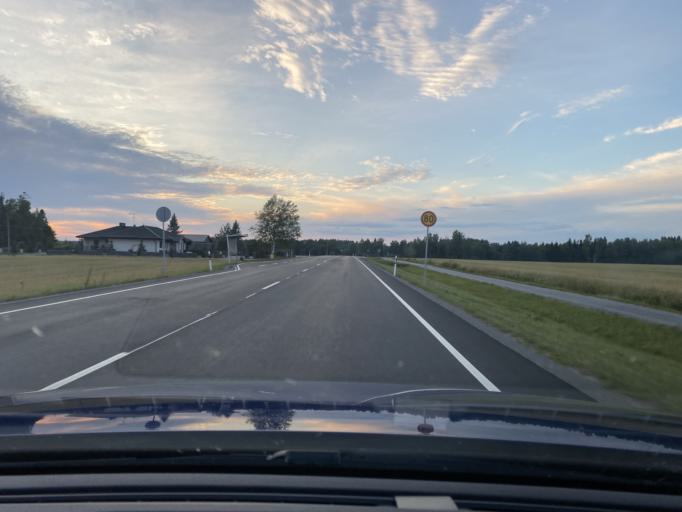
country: FI
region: Satakunta
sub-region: Pohjois-Satakunta
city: Kankaanpaeae
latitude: 61.8494
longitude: 22.3318
